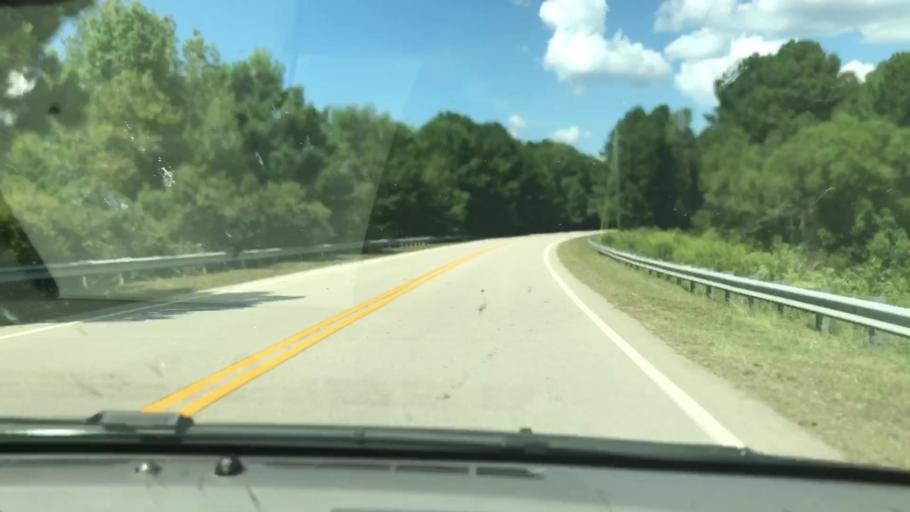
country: US
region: Georgia
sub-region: Troup County
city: La Grange
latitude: 33.1352
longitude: -85.0898
